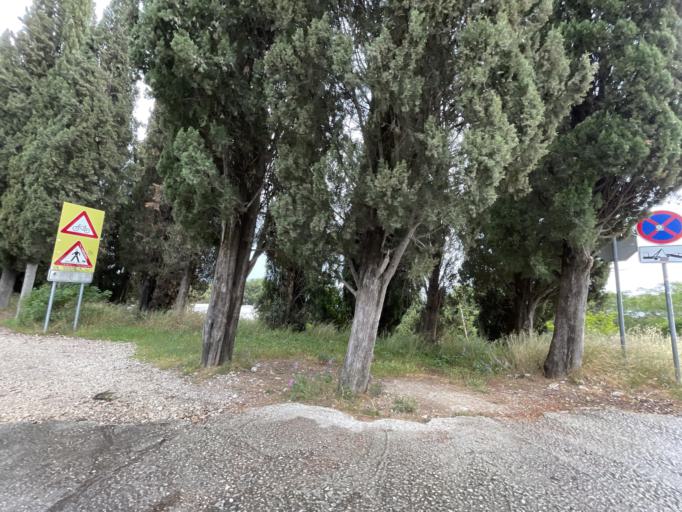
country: HR
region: Splitsko-Dalmatinska
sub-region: Grad Split
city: Split
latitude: 43.5053
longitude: 16.4033
